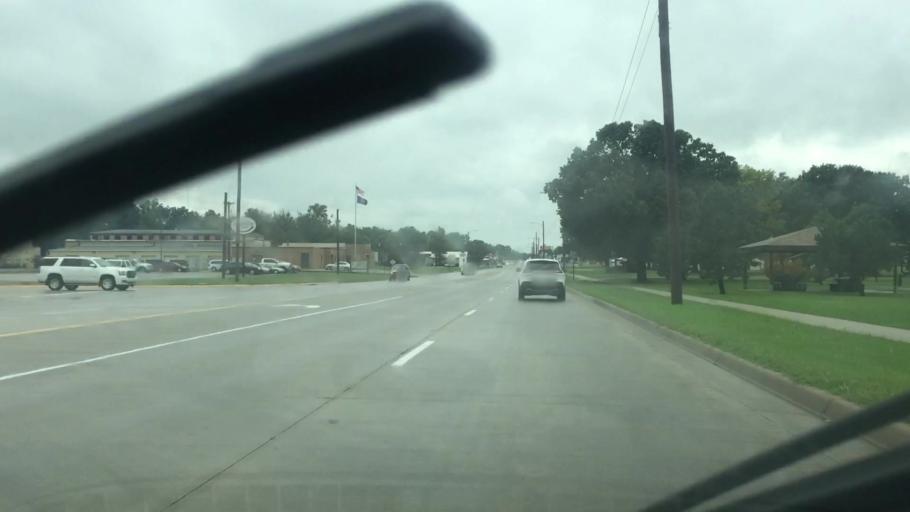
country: US
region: Kansas
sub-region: Allen County
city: Iola
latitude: 37.9337
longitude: -95.4091
